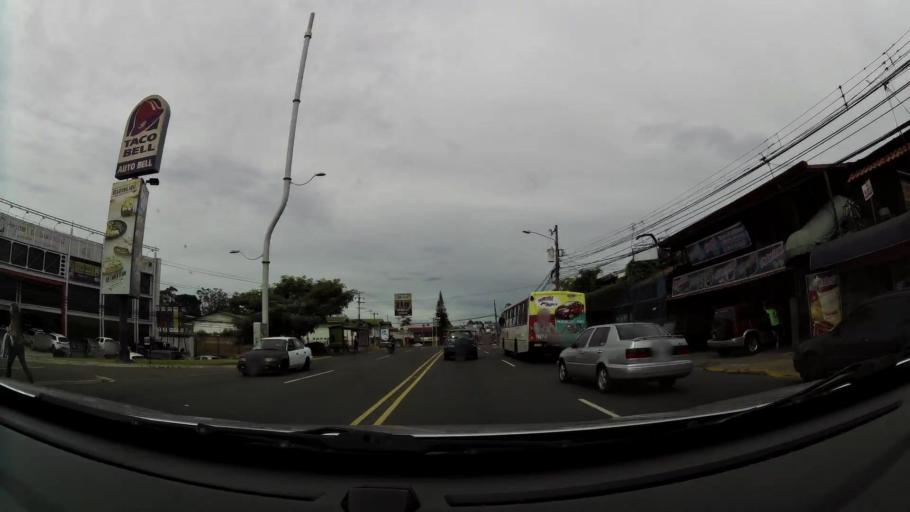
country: CR
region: San Jose
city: Curridabat
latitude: 9.9189
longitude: -84.0346
